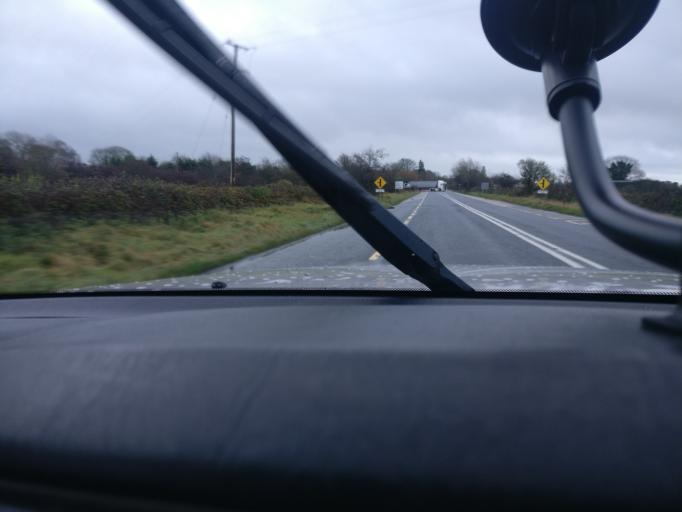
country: IE
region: Leinster
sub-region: An Mhi
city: Longwood
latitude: 53.4258
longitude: -6.8936
